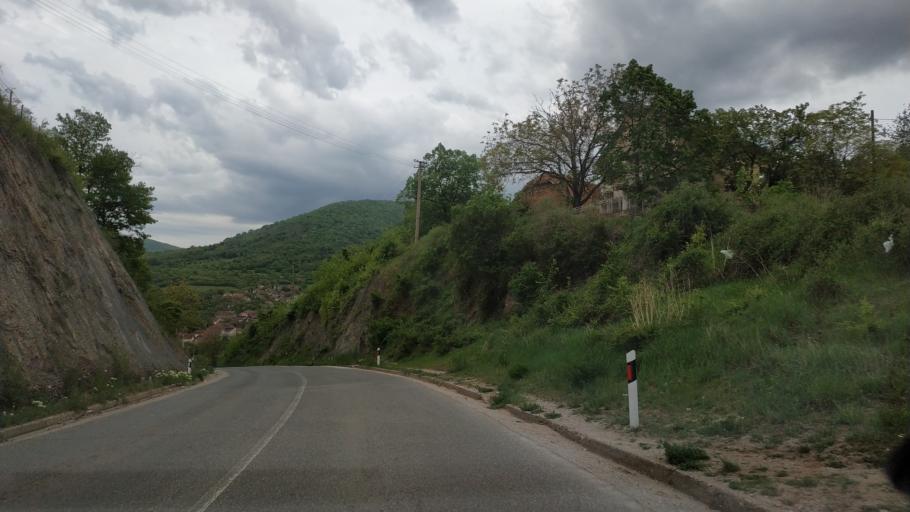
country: RS
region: Central Serbia
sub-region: Nisavski Okrug
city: Aleksinac
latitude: 43.6387
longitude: 21.7138
